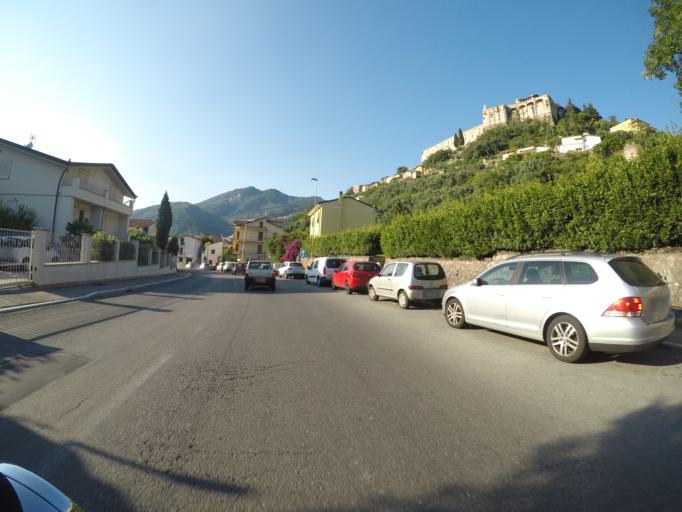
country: IT
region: Tuscany
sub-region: Provincia di Massa-Carrara
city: Massa
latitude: 44.0307
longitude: 10.1444
